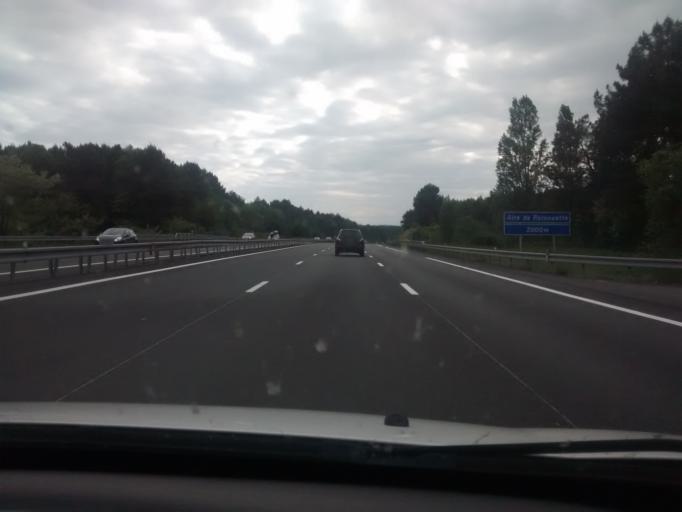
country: FR
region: Pays de la Loire
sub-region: Departement de la Sarthe
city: Connerre
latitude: 48.0779
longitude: 0.4824
